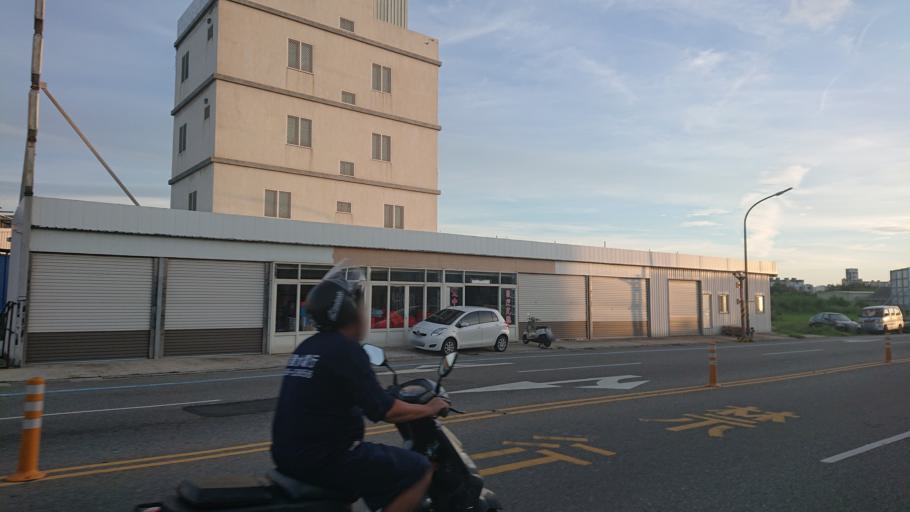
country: TW
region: Taiwan
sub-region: Penghu
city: Ma-kung
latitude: 23.5692
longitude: 119.5893
